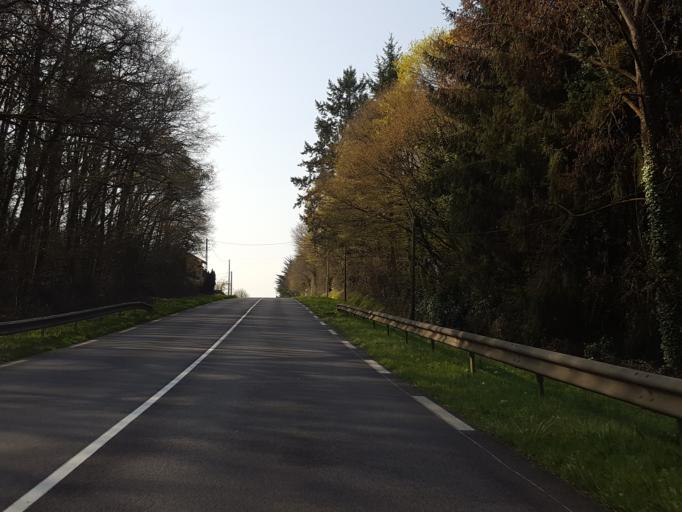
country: FR
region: Pays de la Loire
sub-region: Departement de la Vendee
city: Rocheserviere
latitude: 46.9025
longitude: -1.5030
